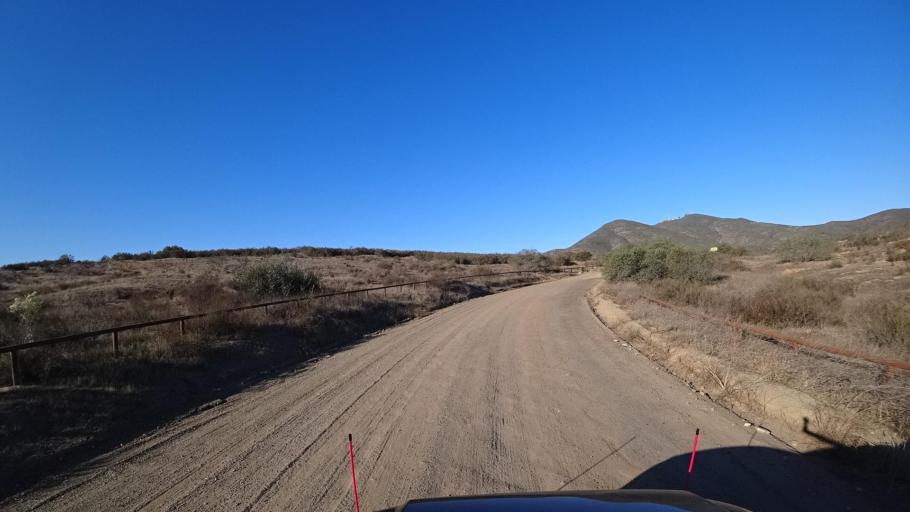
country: US
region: California
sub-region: San Diego County
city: Jamul
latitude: 32.6926
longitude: -116.9034
